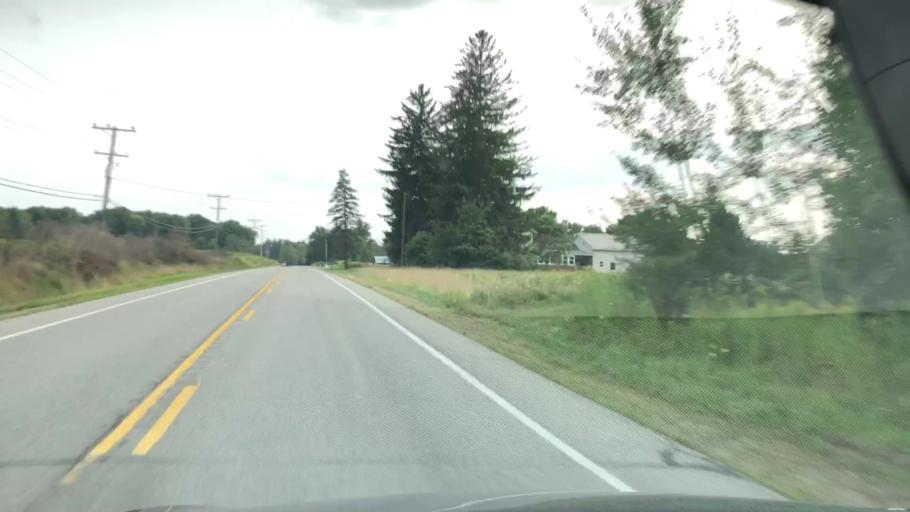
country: US
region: Pennsylvania
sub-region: Crawford County
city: Titusville
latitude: 41.5956
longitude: -79.6813
